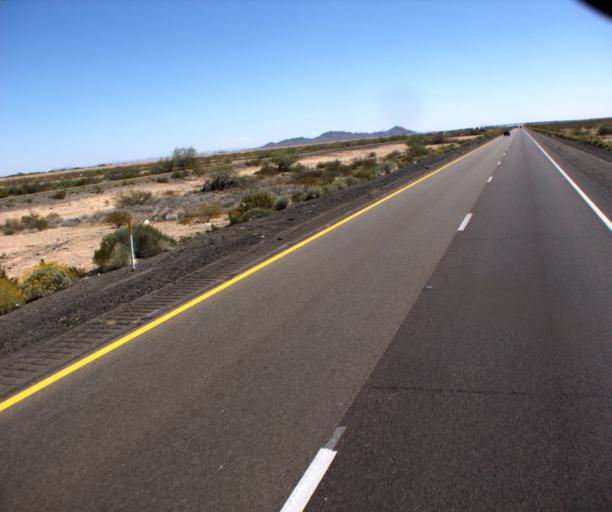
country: US
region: Arizona
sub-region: La Paz County
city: Salome
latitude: 33.5985
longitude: -113.5507
